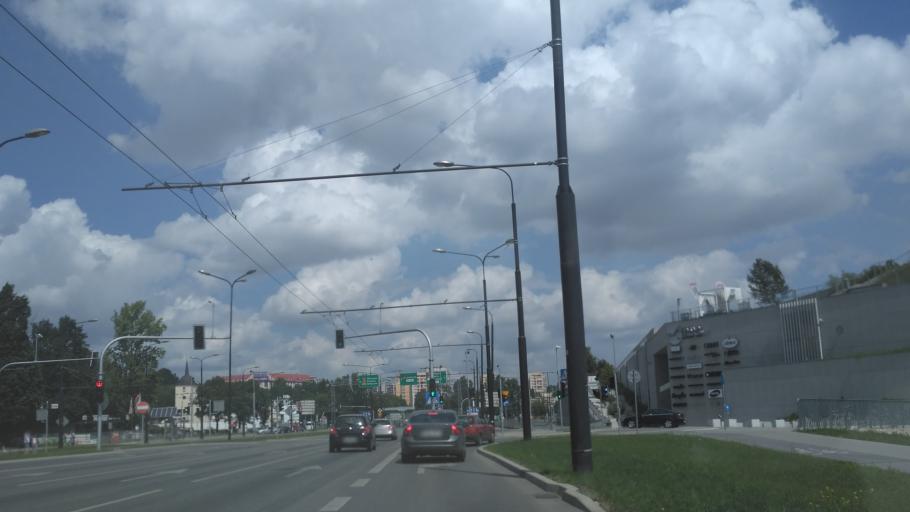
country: PL
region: Lublin Voivodeship
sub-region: Powiat lubelski
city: Lublin
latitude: 51.2487
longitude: 22.5746
